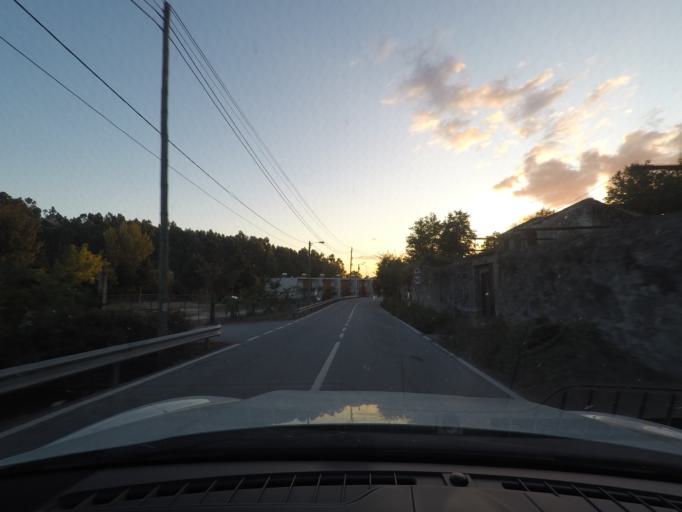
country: PT
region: Braga
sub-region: Fafe
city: Fafe
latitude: 41.4461
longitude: -8.1569
